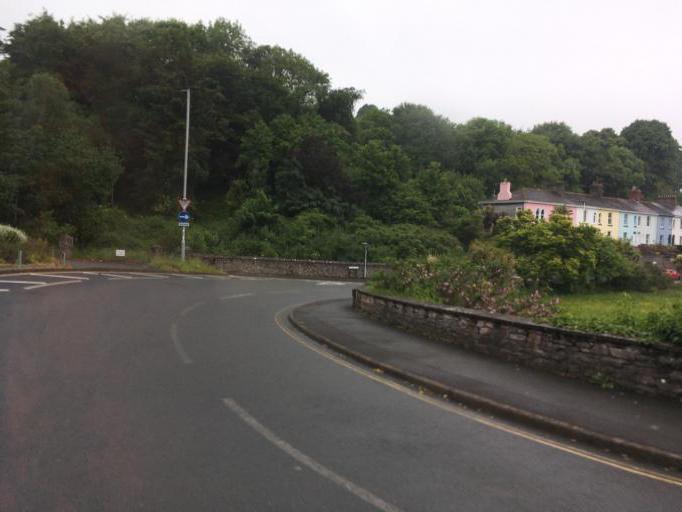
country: GB
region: England
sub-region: Devon
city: Dartmouth
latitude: 50.3547
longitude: -3.5786
